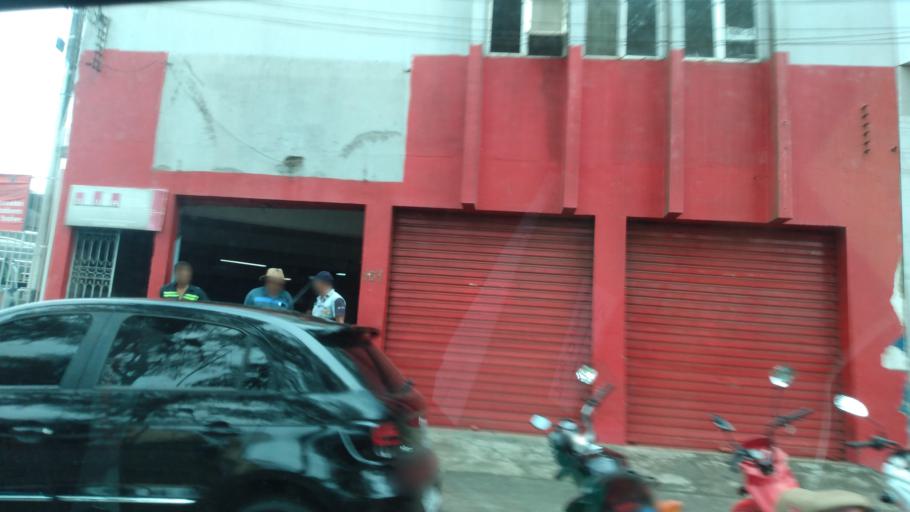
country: BR
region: Pernambuco
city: Garanhuns
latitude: -8.8848
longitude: -36.4891
